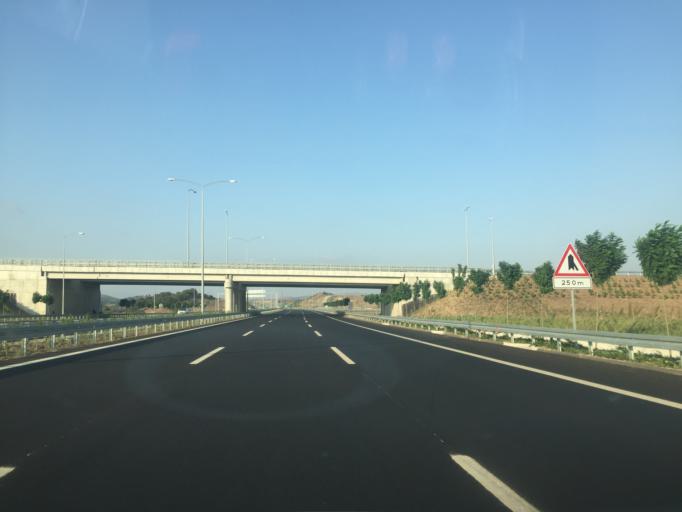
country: TR
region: Balikesir
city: Ertugrul
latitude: 39.6369
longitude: 27.7135
